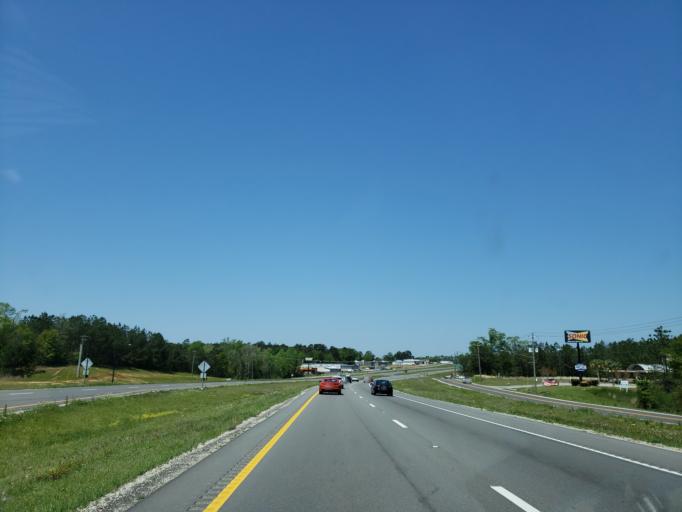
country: US
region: Mississippi
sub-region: Stone County
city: Wiggins
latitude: 30.8449
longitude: -89.1489
